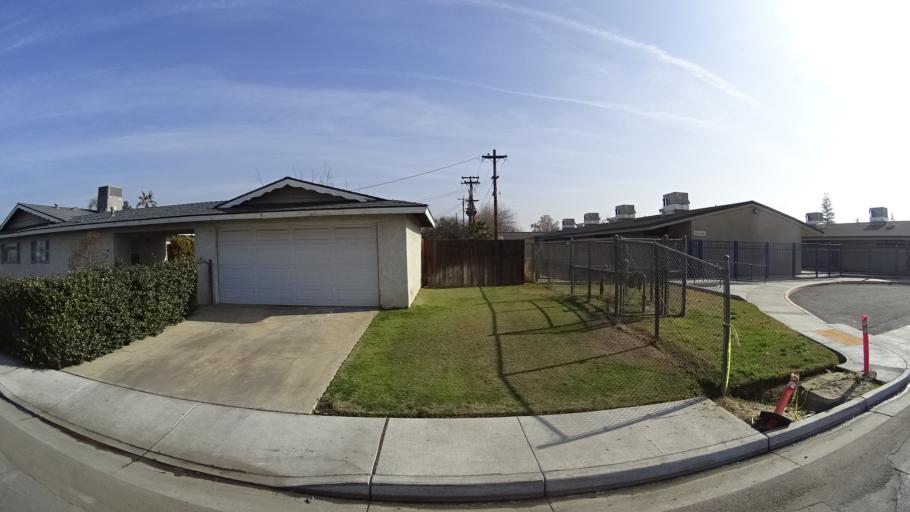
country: US
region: California
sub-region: Kern County
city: Bakersfield
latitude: 35.3303
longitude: -119.0351
